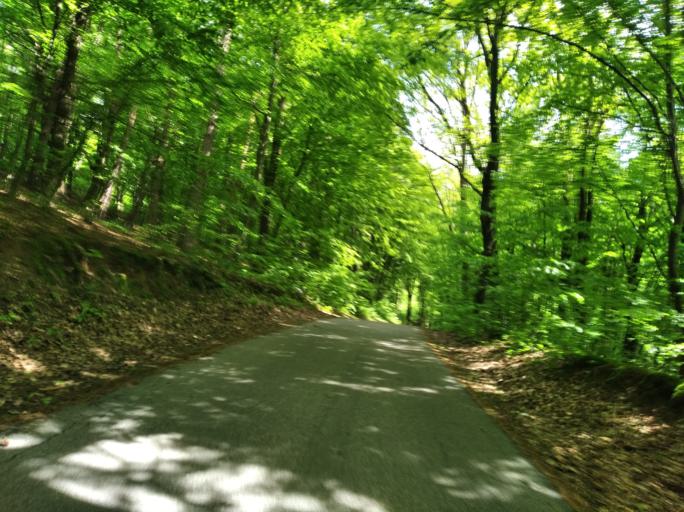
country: PL
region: Subcarpathian Voivodeship
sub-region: Powiat strzyzowski
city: Czudec
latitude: 49.9272
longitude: 21.8237
